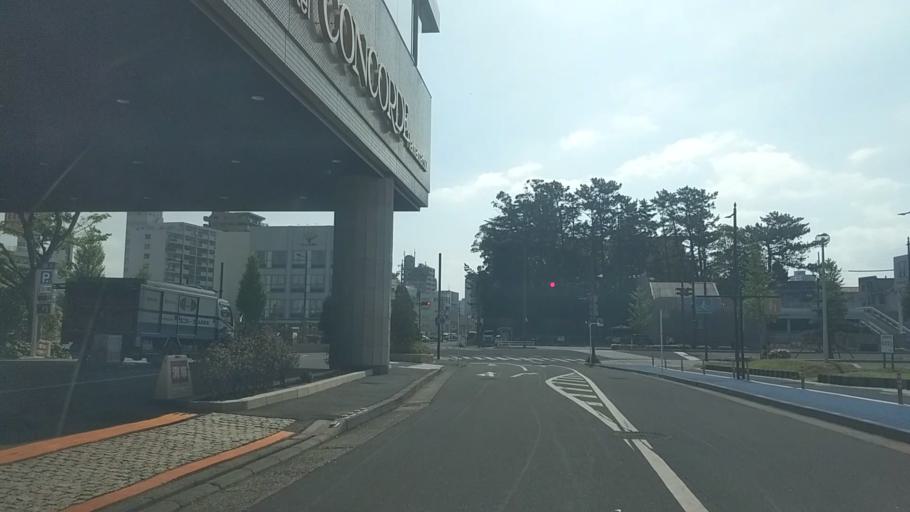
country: JP
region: Shizuoka
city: Hamamatsu
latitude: 34.7137
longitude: 137.7270
